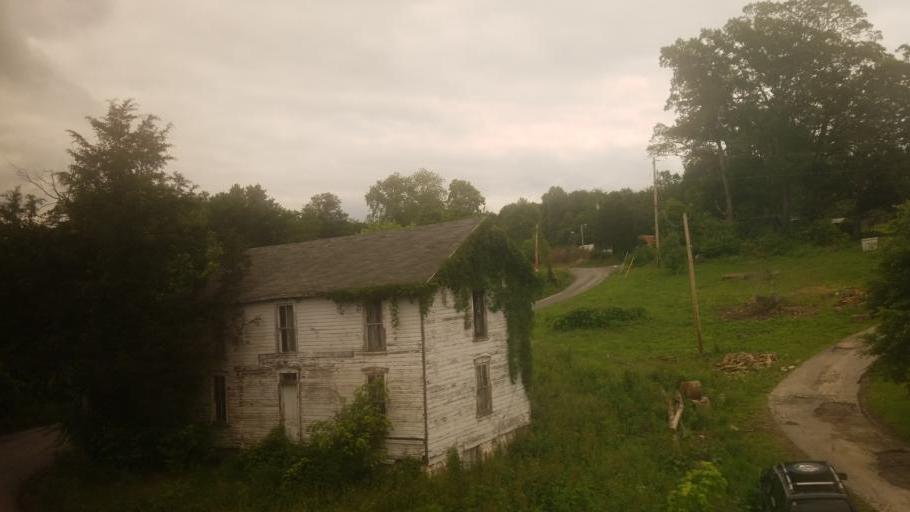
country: US
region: West Virginia
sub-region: Morgan County
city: Berkeley Springs
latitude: 39.6246
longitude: -78.3793
